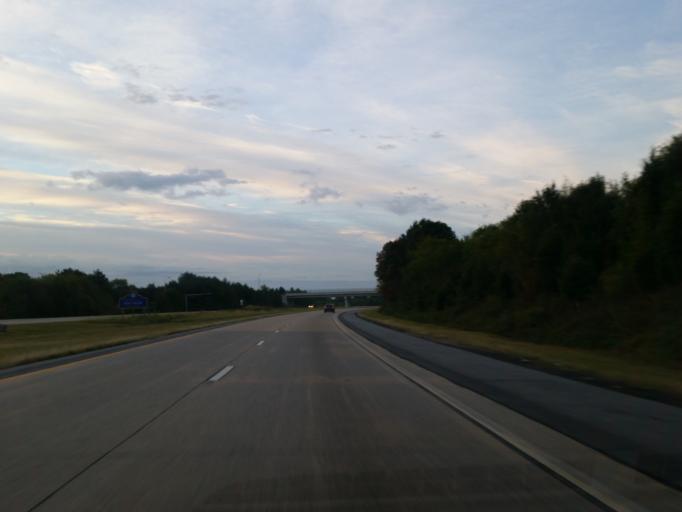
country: US
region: Delaware
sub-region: Kent County
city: Smyrna
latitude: 39.3085
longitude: -75.5962
